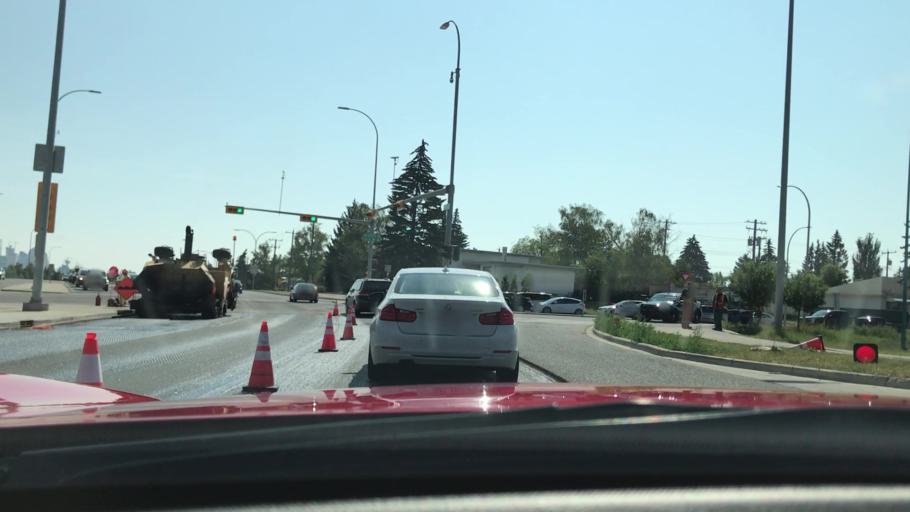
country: CA
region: Alberta
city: Calgary
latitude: 51.0417
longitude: -114.1362
